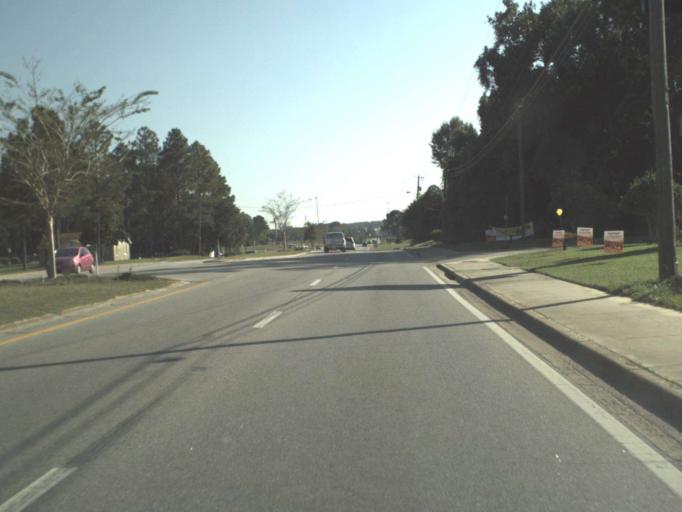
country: US
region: Florida
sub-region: Walton County
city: DeFuniak Springs
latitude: 30.7007
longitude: -86.1226
